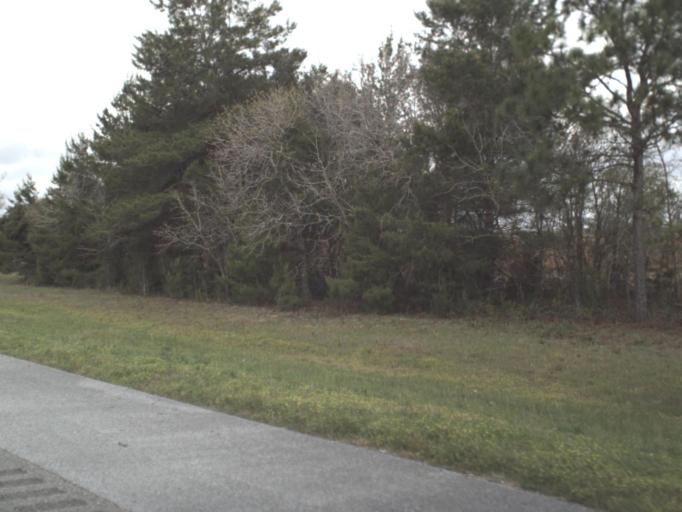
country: US
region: Florida
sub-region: Okaloosa County
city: Crestview
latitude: 30.7181
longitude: -86.4514
